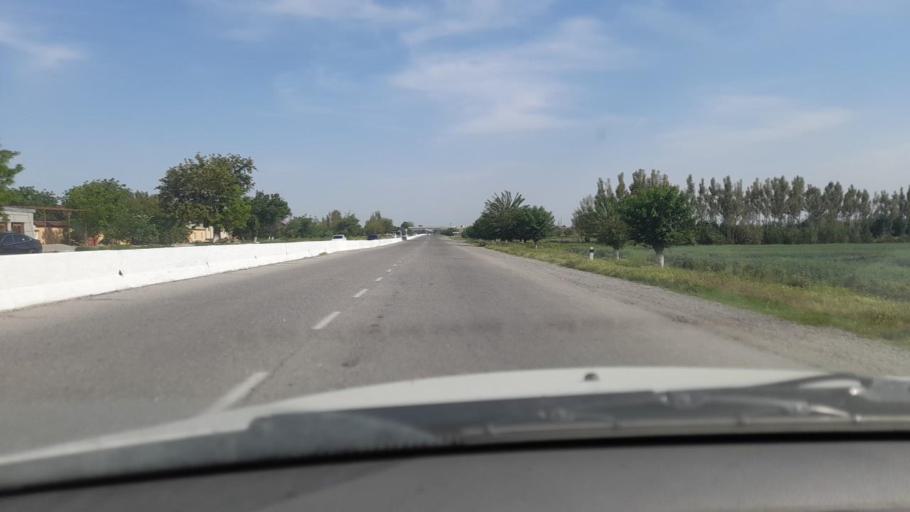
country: UZ
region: Samarqand
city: Daxbet
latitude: 39.7761
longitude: 66.8913
